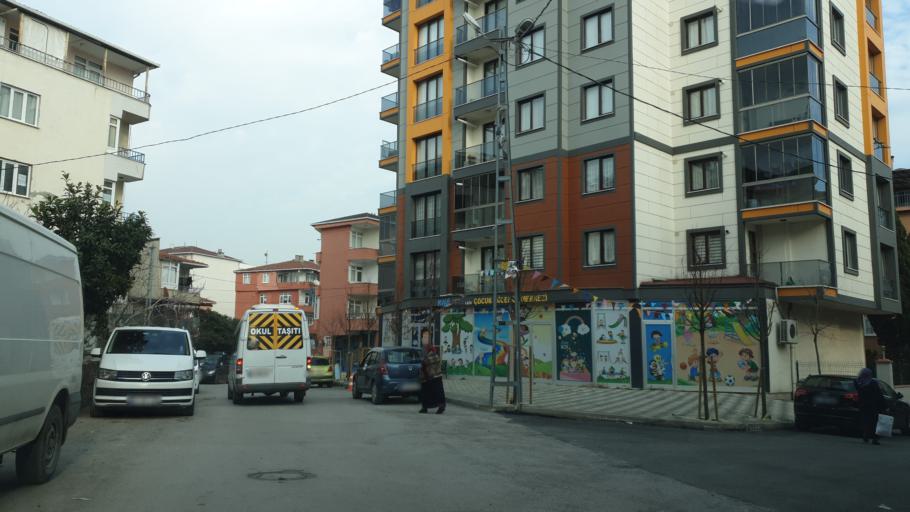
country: TR
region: Istanbul
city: Pendik
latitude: 40.8766
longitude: 29.2737
